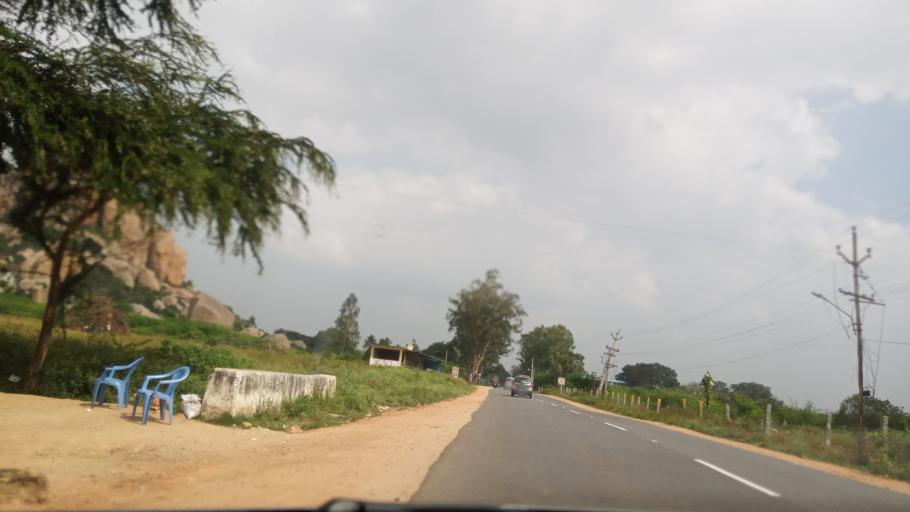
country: IN
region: Andhra Pradesh
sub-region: Chittoor
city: Madanapalle
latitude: 13.6341
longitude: 78.6195
